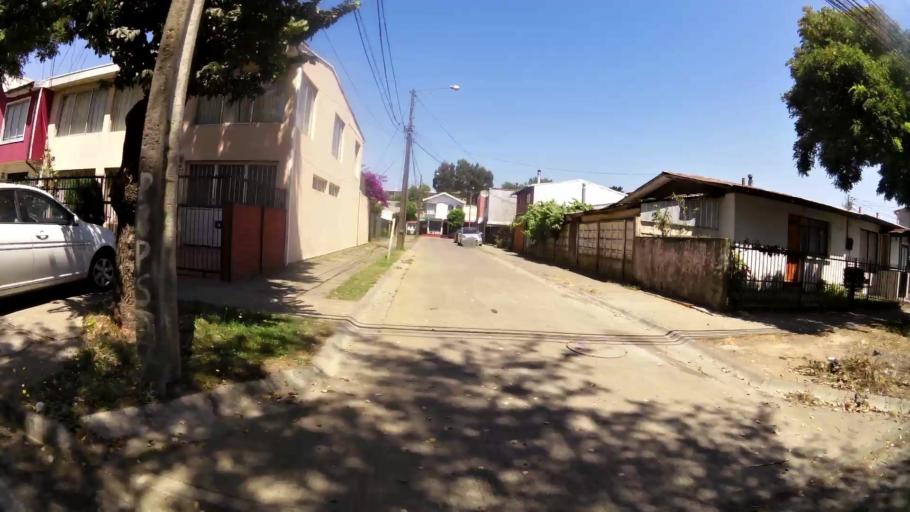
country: CL
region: Biobio
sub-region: Provincia de Concepcion
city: Concepcion
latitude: -36.8066
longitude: -73.0633
